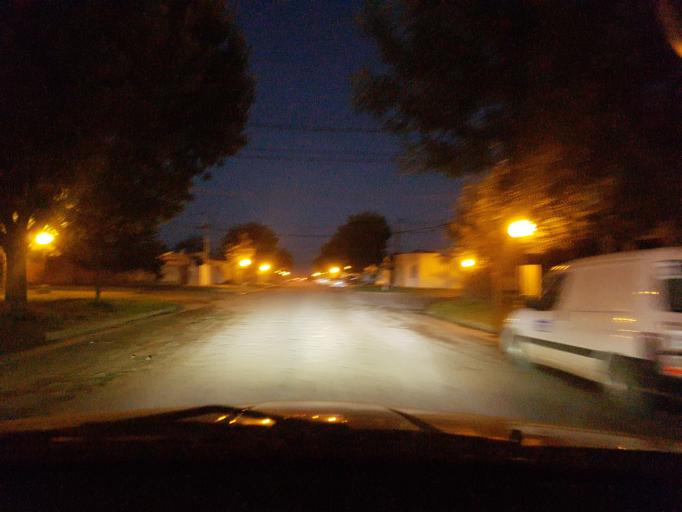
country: AR
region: Cordoba
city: Las Perdices
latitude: -32.7579
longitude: -63.7755
